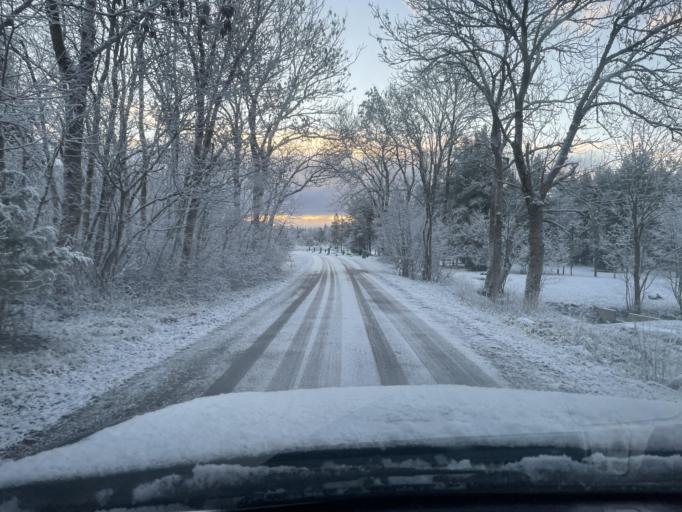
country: EE
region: Harju
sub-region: Keila linn
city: Keila
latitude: 59.3126
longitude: 24.2754
